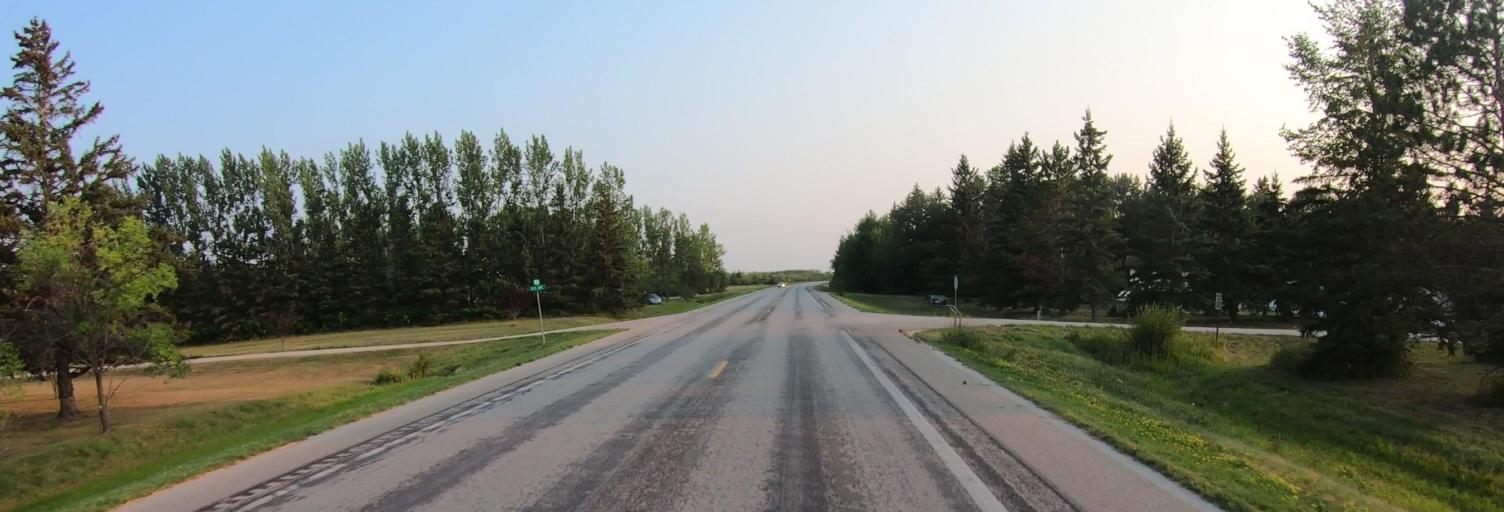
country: US
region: Minnesota
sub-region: Roseau County
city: Warroad
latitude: 48.8765
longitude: -95.3209
